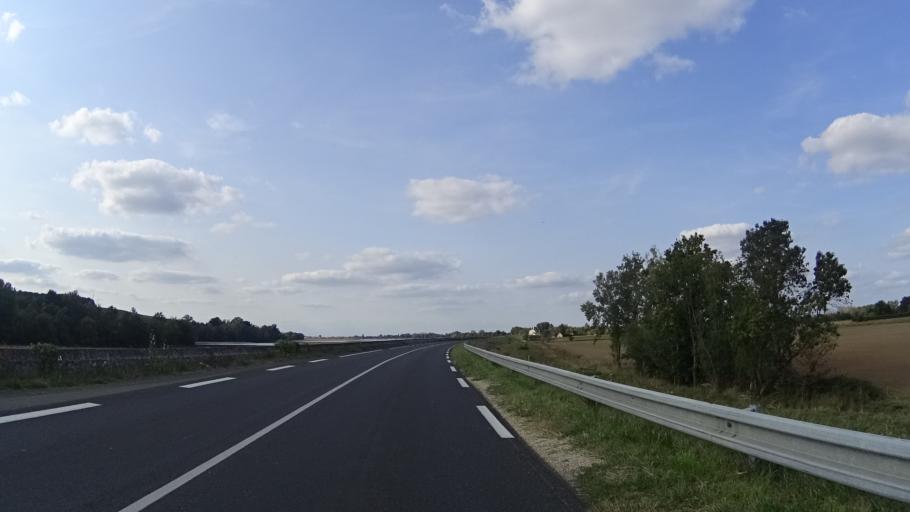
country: FR
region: Pays de la Loire
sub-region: Departement de Maine-et-Loire
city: La Menitre
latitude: 47.3843
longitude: -0.2673
